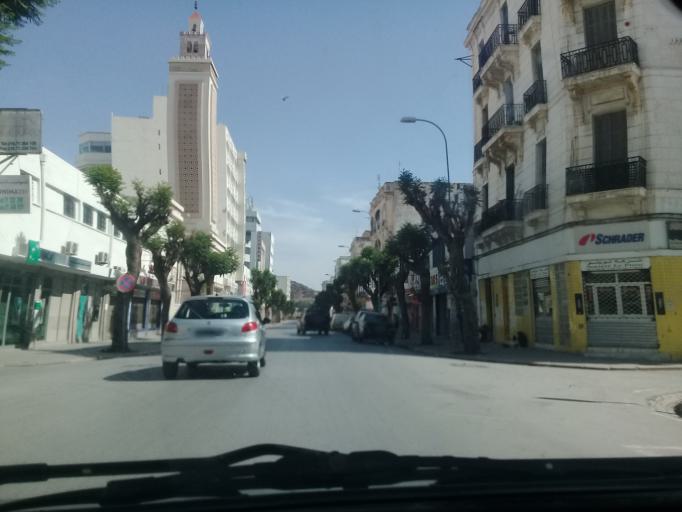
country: TN
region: Tunis
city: Tunis
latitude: 36.7945
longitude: 10.1823
